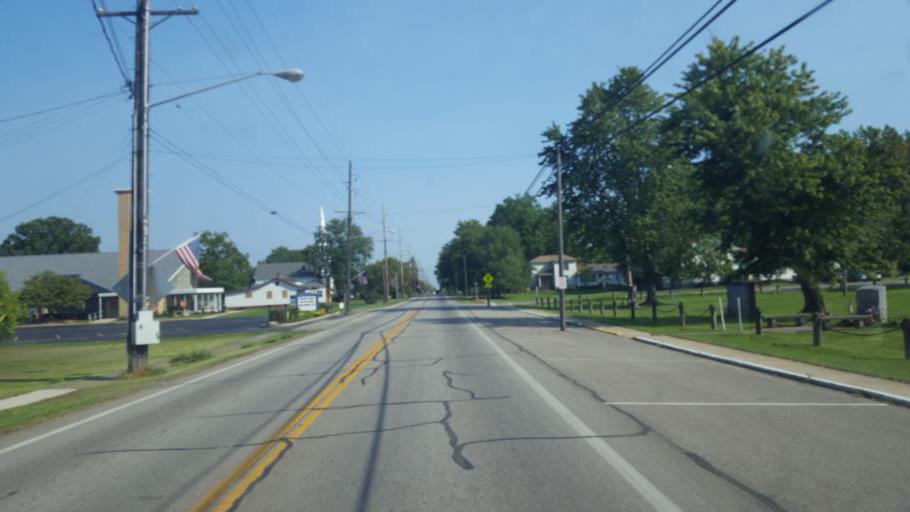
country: US
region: Ohio
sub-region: Ashtabula County
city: Orwell
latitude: 41.5371
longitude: -80.8677
